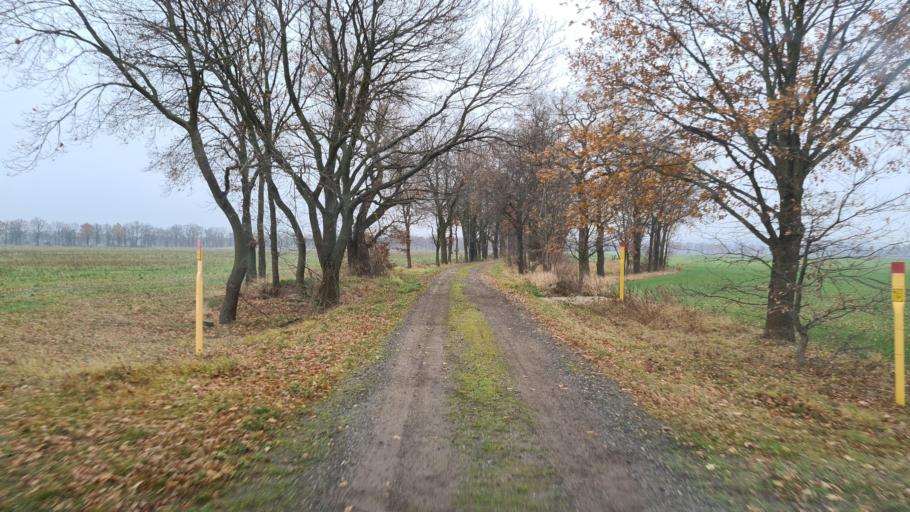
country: DE
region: Brandenburg
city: Schraden
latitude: 51.4147
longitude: 13.7039
